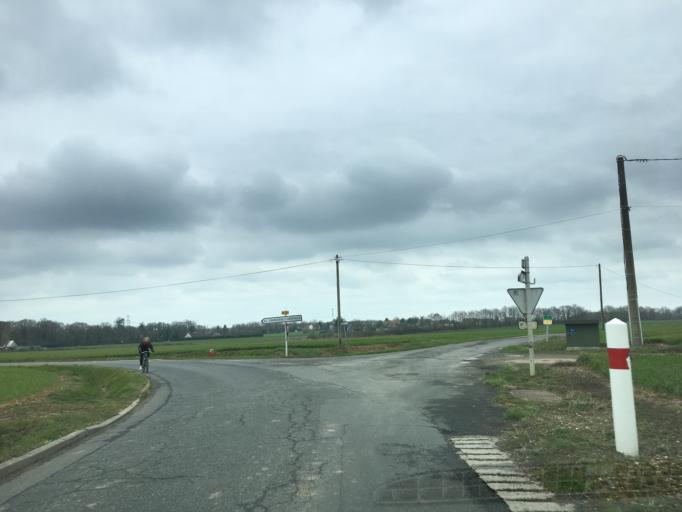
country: FR
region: Centre
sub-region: Departement d'Indre-et-Loire
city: Parcay-Meslay
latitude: 47.4698
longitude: 0.7361
